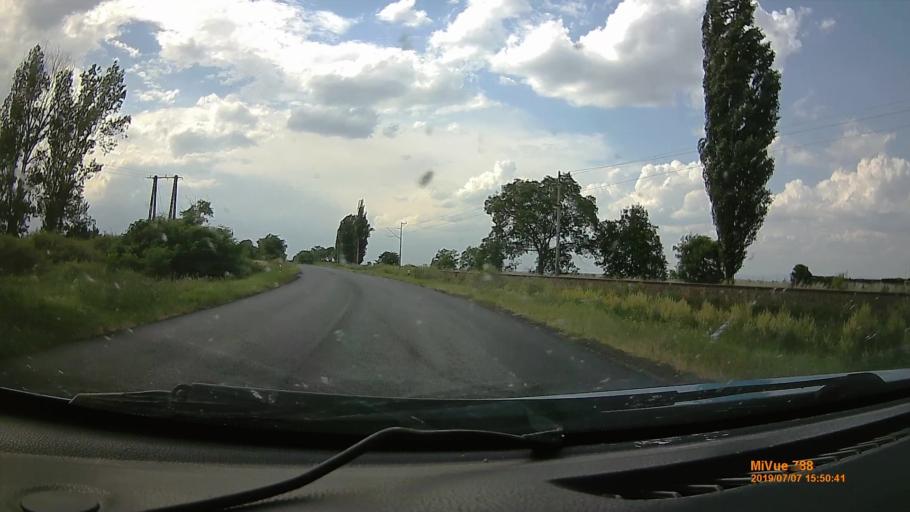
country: HU
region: Jasz-Nagykun-Szolnok
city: Jaszbereny
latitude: 47.5278
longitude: 19.8506
